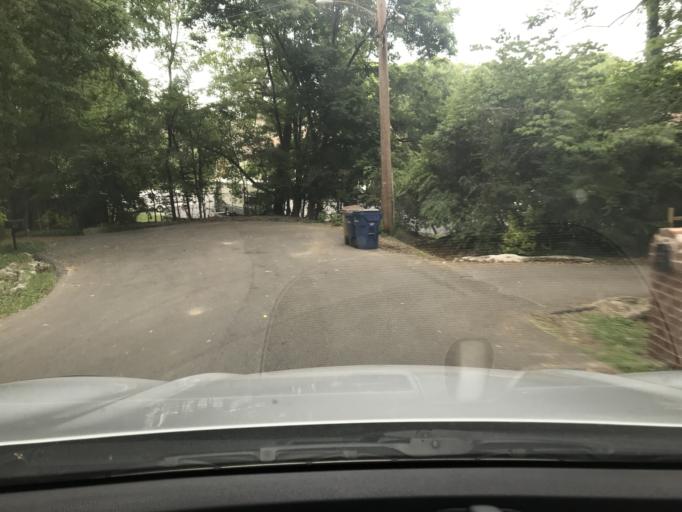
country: US
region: Tennessee
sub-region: Davidson County
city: Goodlettsville
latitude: 36.3095
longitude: -86.7086
